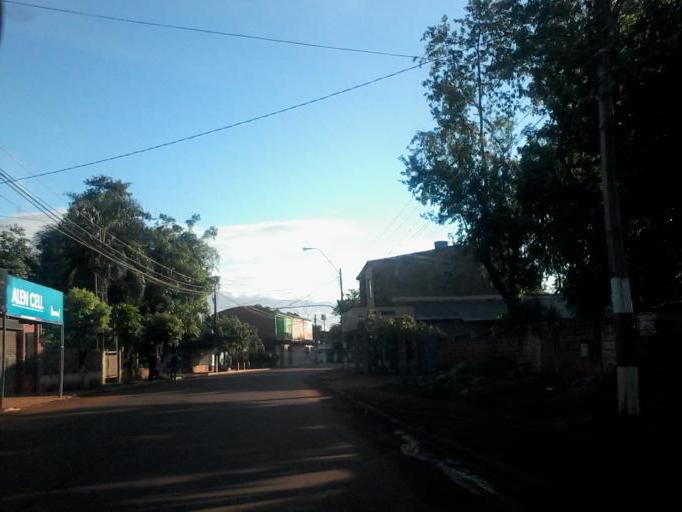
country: PY
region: Alto Parana
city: Ciudad del Este
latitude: -25.4356
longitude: -54.6404
